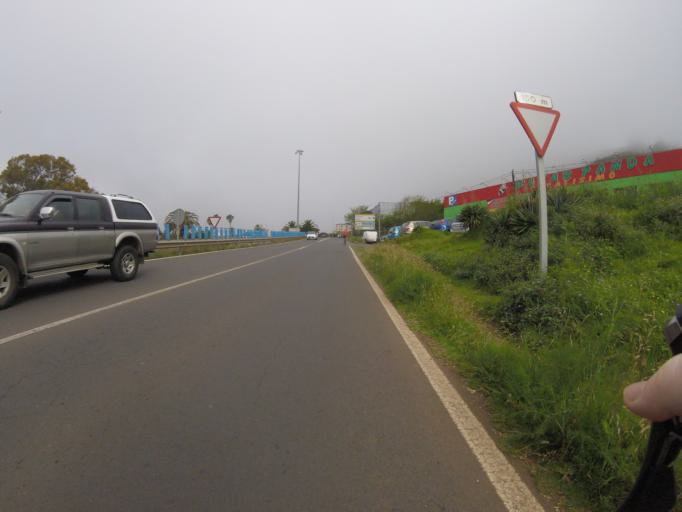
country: ES
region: Canary Islands
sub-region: Provincia de Santa Cruz de Tenerife
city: La Laguna
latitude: 28.4897
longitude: -16.3473
